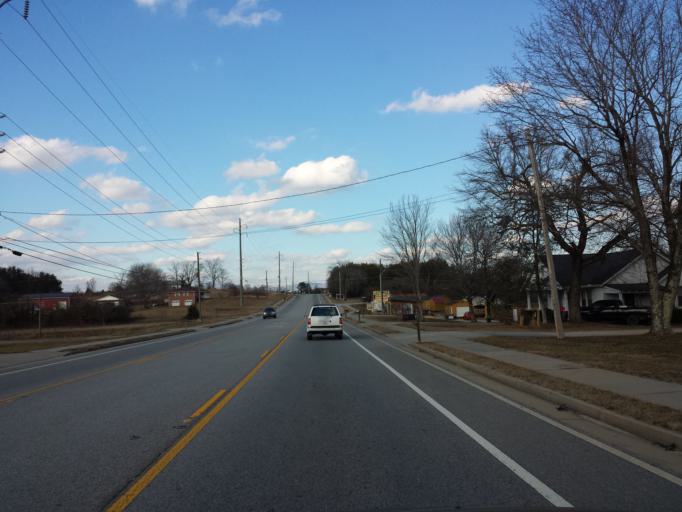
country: US
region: Georgia
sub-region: White County
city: Cleveland
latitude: 34.6236
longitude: -83.7533
